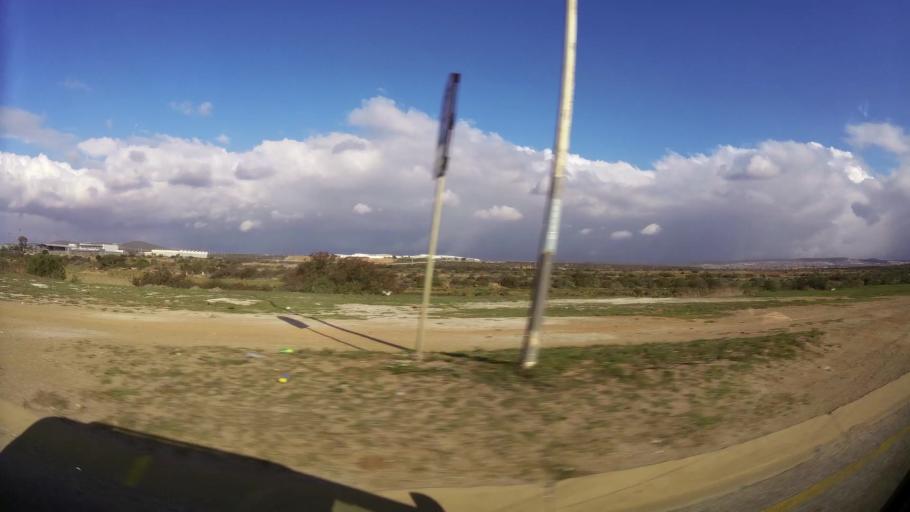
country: ZA
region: Eastern Cape
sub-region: Nelson Mandela Bay Metropolitan Municipality
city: Uitenhage
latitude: -33.7910
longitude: 25.4177
